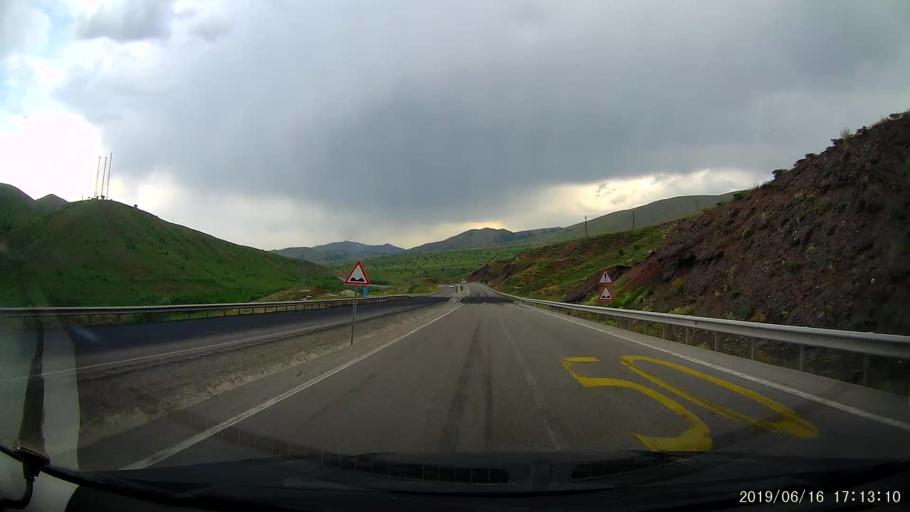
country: TR
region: Erzurum
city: Askale
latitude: 39.8598
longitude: 40.6046
